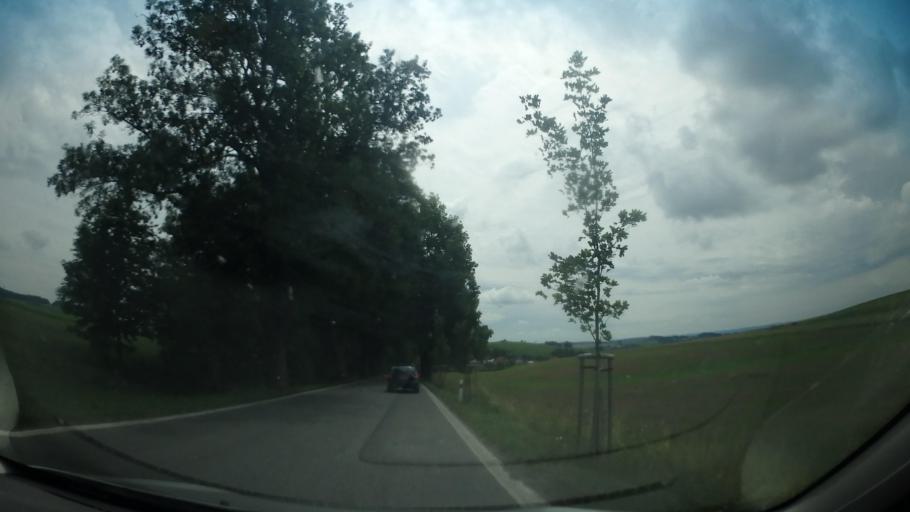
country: CZ
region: Vysocina
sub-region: Okres Zd'ar nad Sazavou
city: Nove Mesto na Morave
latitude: 49.5865
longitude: 16.0761
